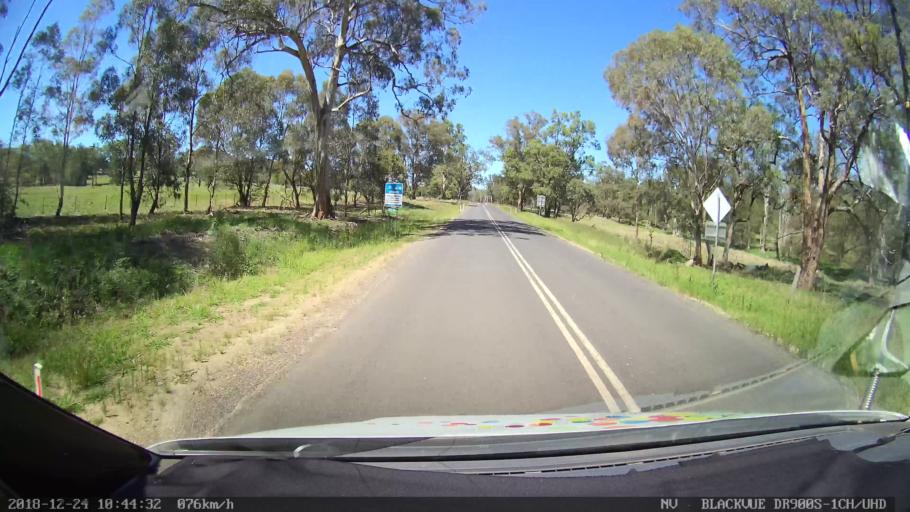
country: AU
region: New South Wales
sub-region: Upper Hunter Shire
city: Merriwa
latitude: -31.8940
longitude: 150.4432
